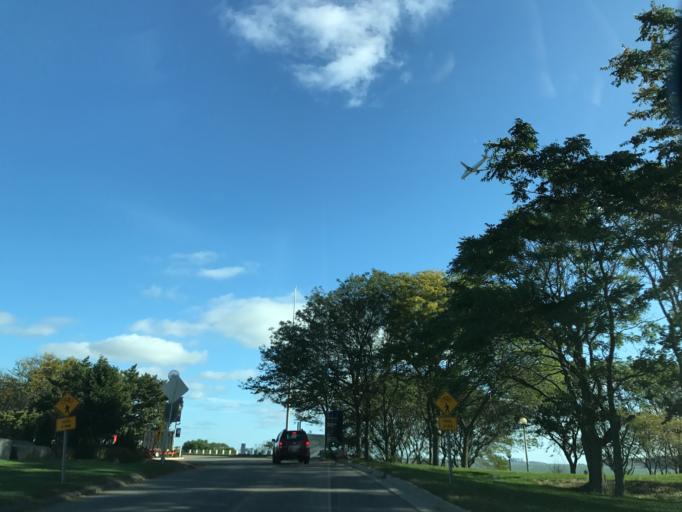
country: US
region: Massachusetts
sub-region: Suffolk County
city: South Boston
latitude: 42.3134
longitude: -71.0339
